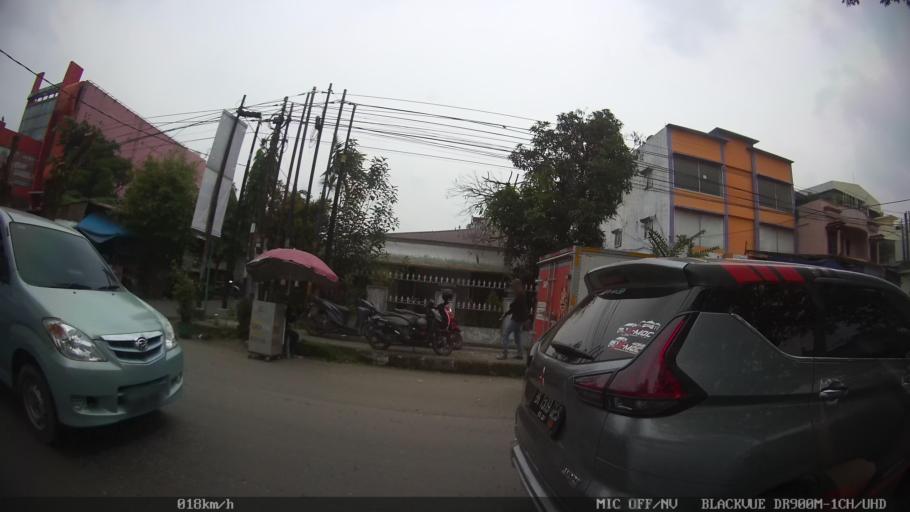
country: ID
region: North Sumatra
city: Deli Tua
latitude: 3.5479
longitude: 98.6984
